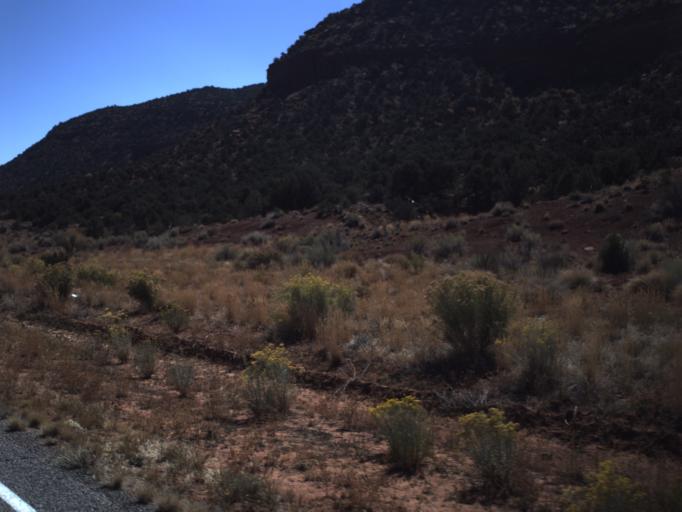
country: US
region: Utah
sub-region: San Juan County
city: Blanding
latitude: 37.6048
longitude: -110.0652
